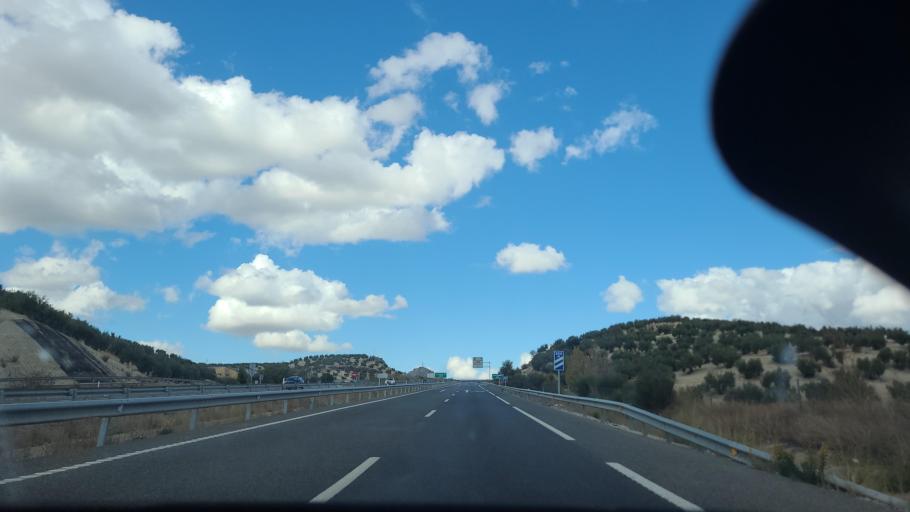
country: ES
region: Andalusia
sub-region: Provincia de Jaen
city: Noalejo
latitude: 37.5250
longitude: -3.6370
